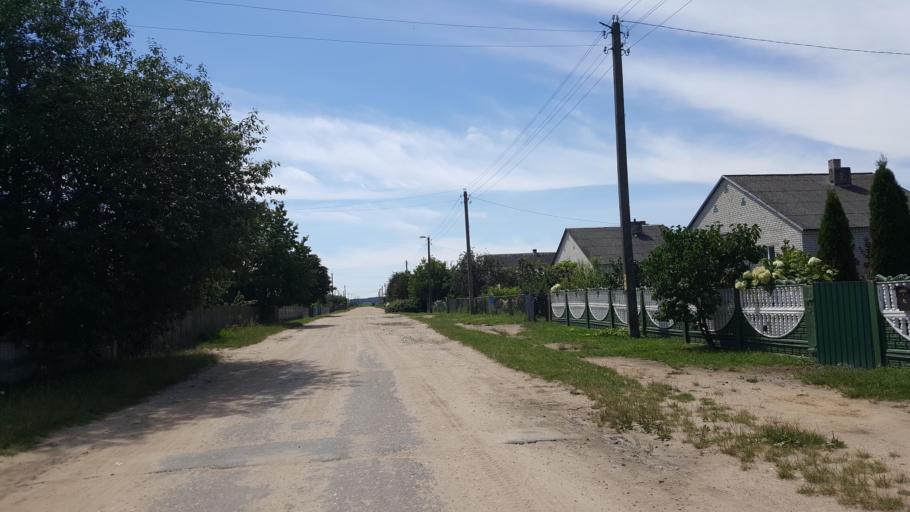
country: BY
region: Brest
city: Pruzhany
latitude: 52.5545
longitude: 24.2066
